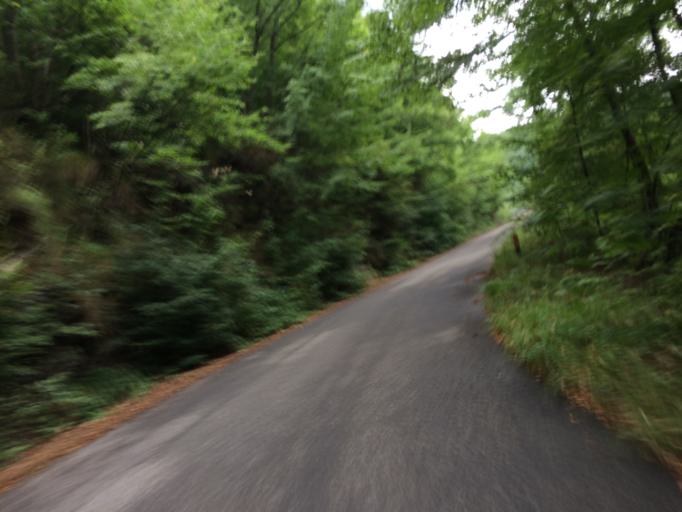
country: IT
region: Liguria
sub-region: Provincia di Imperia
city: Triora
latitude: 43.9795
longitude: 7.7465
